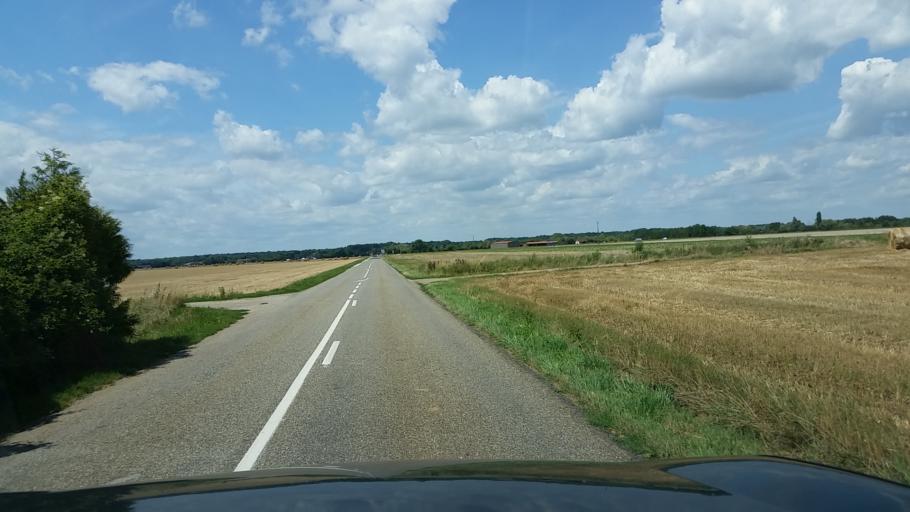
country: FR
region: Franche-Comte
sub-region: Departement du Jura
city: Bletterans
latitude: 46.7482
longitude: 5.4902
